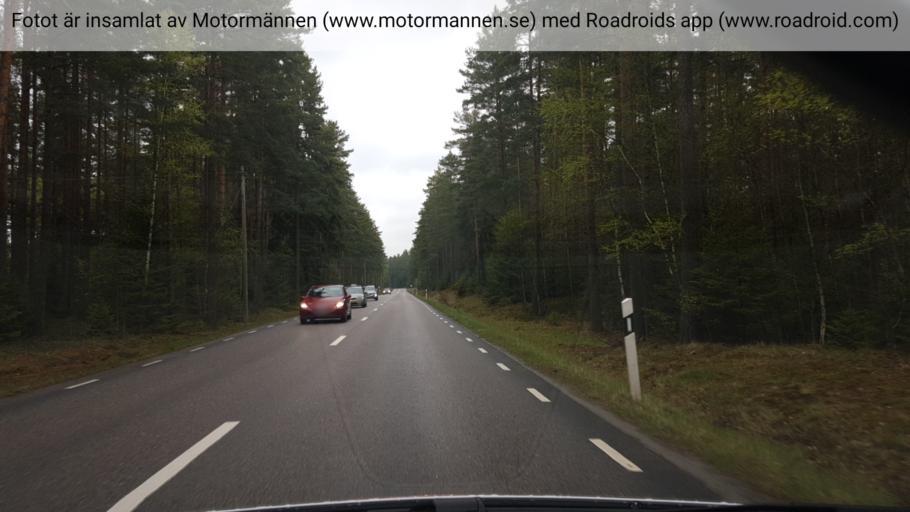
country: SE
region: Vaestra Goetaland
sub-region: Skovde Kommun
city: Stopen
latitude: 58.4613
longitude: 13.9573
